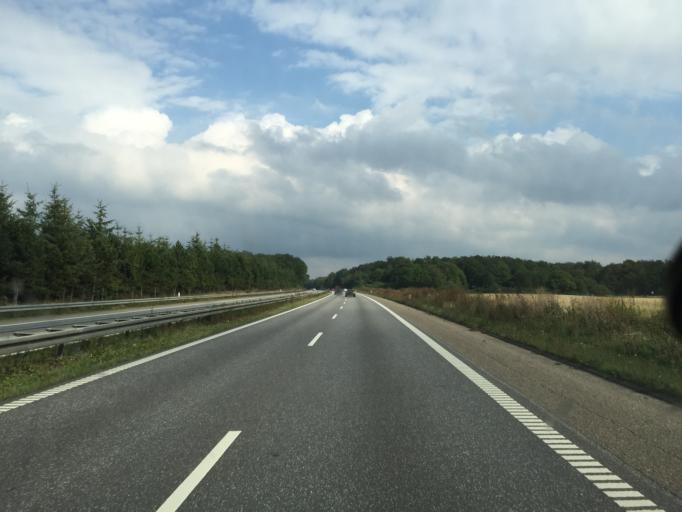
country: DK
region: Zealand
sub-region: Soro Kommune
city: Soro
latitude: 55.4343
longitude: 11.4828
